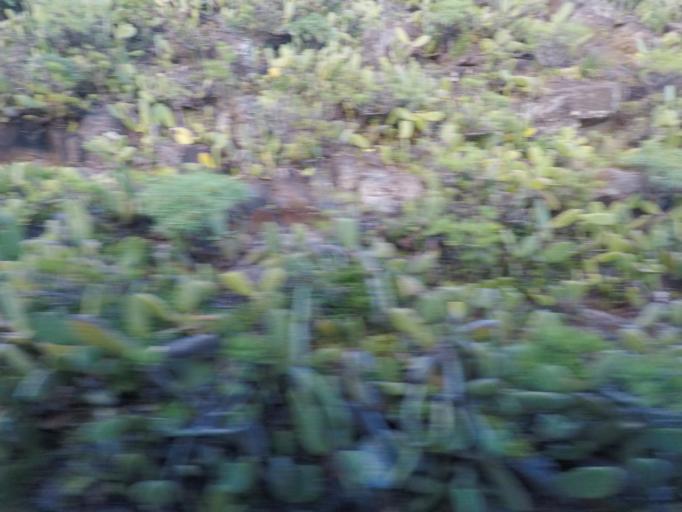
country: ES
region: Canary Islands
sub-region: Provincia de Santa Cruz de Tenerife
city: San Sebastian de la Gomera
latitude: 28.1015
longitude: -17.1682
